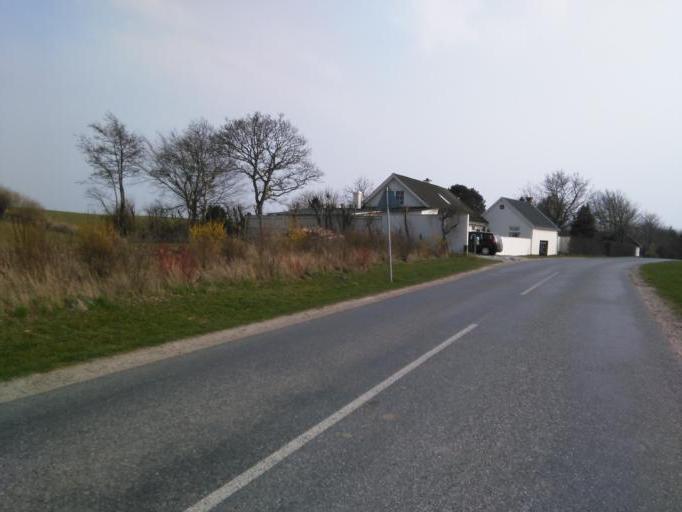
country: DK
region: Central Jutland
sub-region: Arhus Kommune
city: Beder
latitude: 56.0568
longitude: 10.2422
